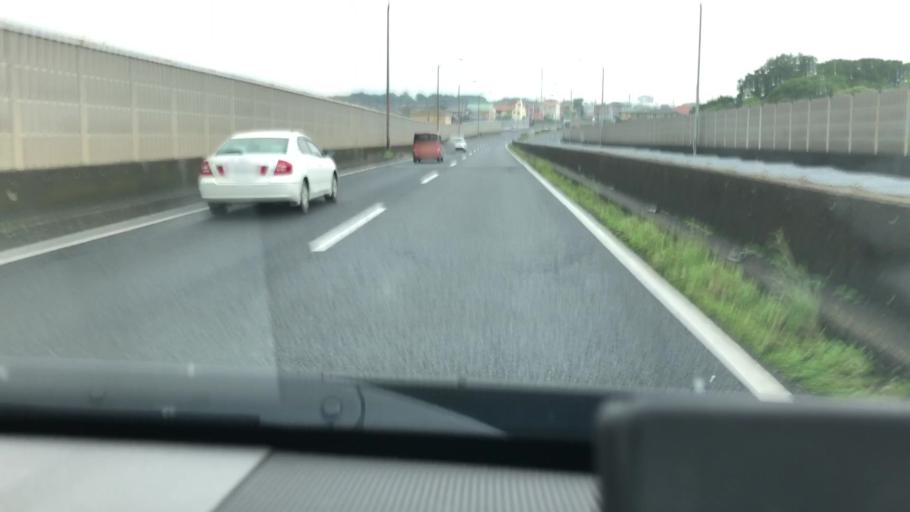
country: JP
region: Chiba
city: Kisarazu
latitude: 35.4369
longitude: 139.9707
